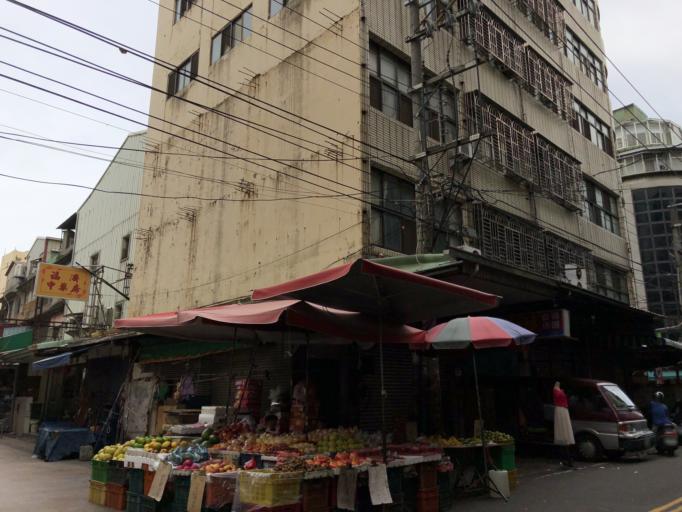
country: TW
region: Taiwan
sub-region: Taichung City
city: Taichung
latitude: 24.2379
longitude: 120.5589
